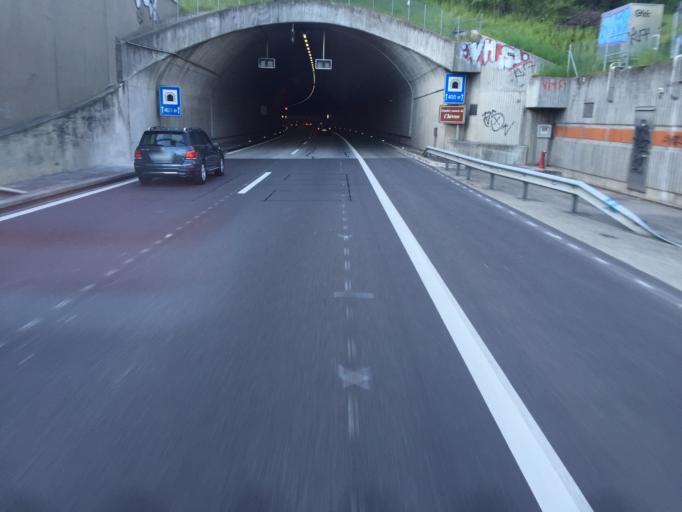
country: CH
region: Geneva
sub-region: Geneva
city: Bernex
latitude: 46.1964
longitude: 6.0783
